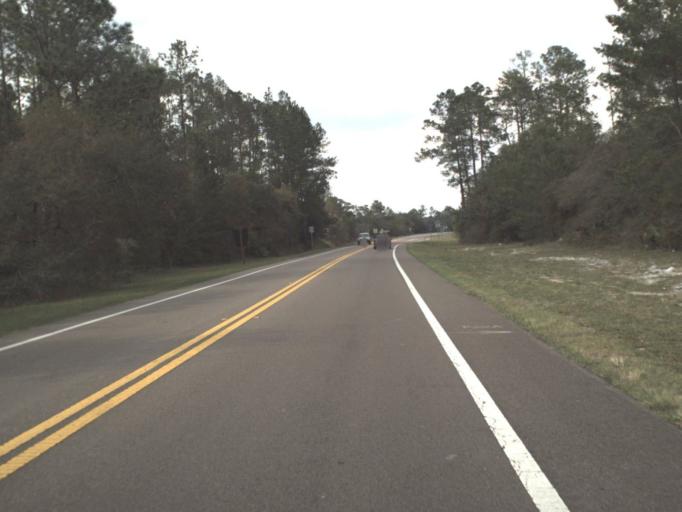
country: US
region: Florida
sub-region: Lake County
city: Umatilla
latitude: 29.0372
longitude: -81.6402
